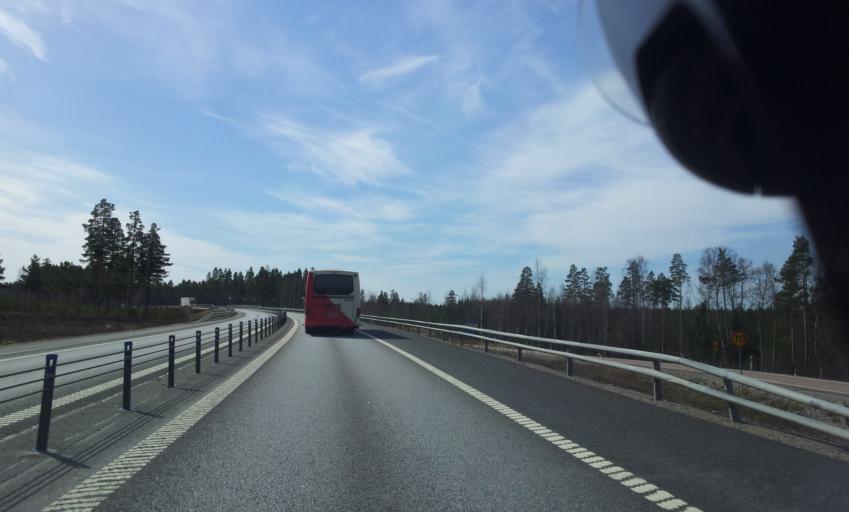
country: SE
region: Gaevleborg
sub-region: Gavle Kommun
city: Norrsundet
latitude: 61.0748
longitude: 16.9656
